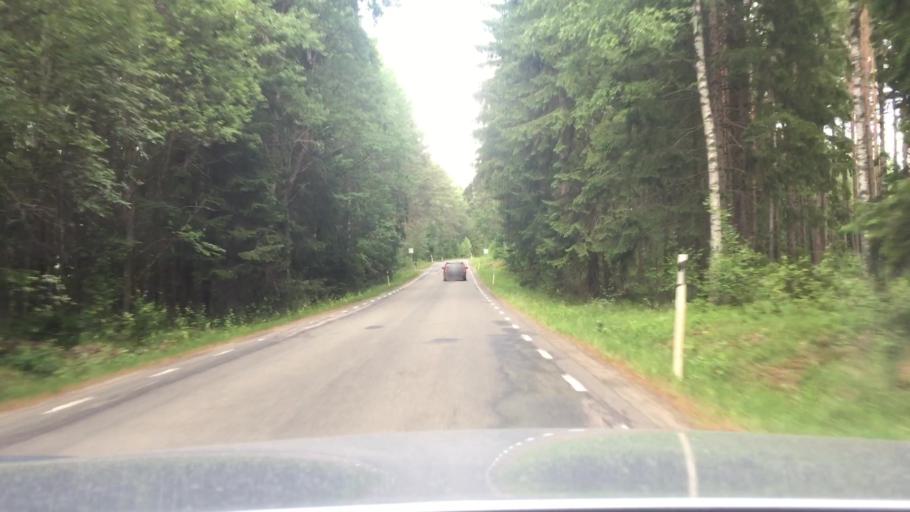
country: SE
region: Vaestra Goetaland
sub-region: Tidaholms Kommun
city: Tidaholm
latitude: 58.2023
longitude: 13.9801
